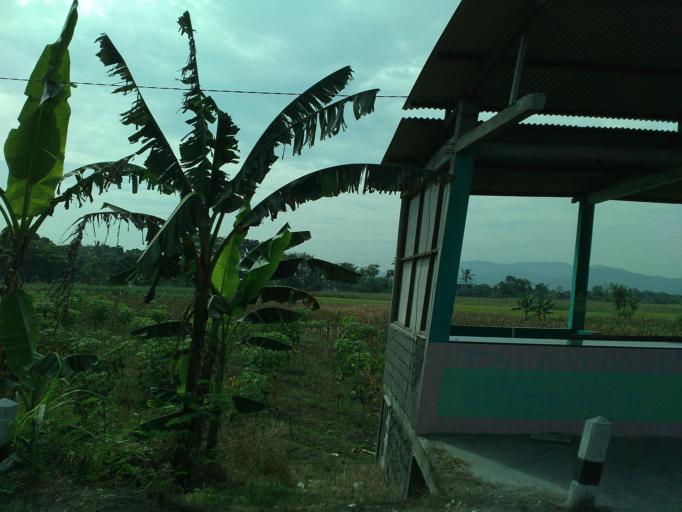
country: ID
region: Central Java
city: Candi Prambanan
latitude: -7.7472
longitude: 110.5244
